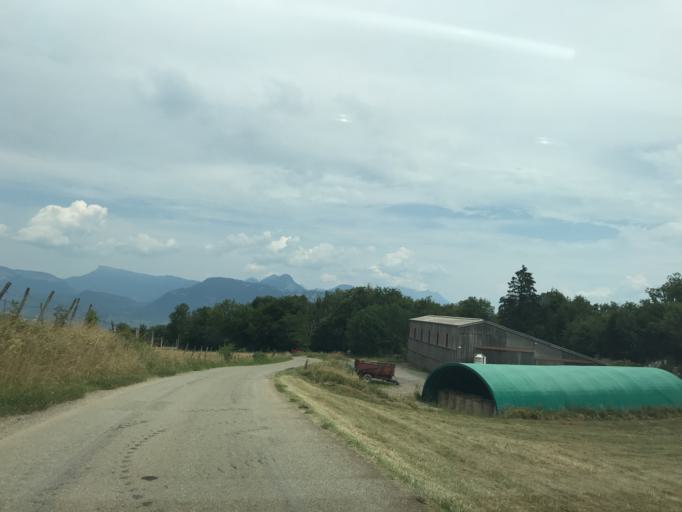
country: FR
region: Rhone-Alpes
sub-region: Departement de l'Isere
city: Barraux
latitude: 45.4456
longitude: 5.9654
